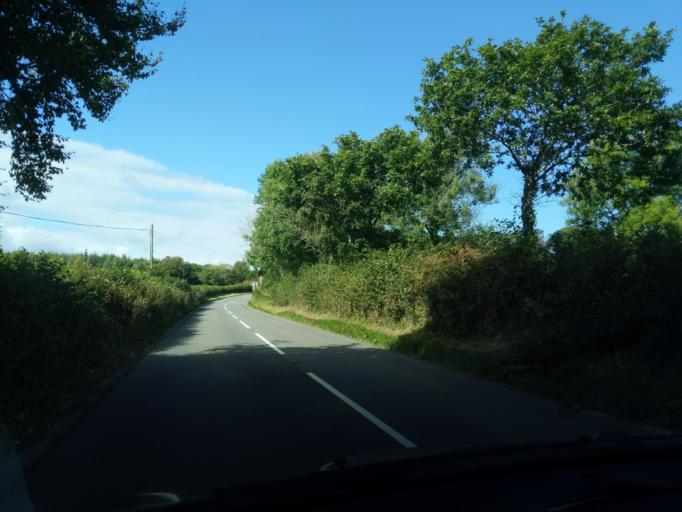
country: GB
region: England
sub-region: Cornwall
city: Werrington
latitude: 50.6975
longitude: -4.3220
